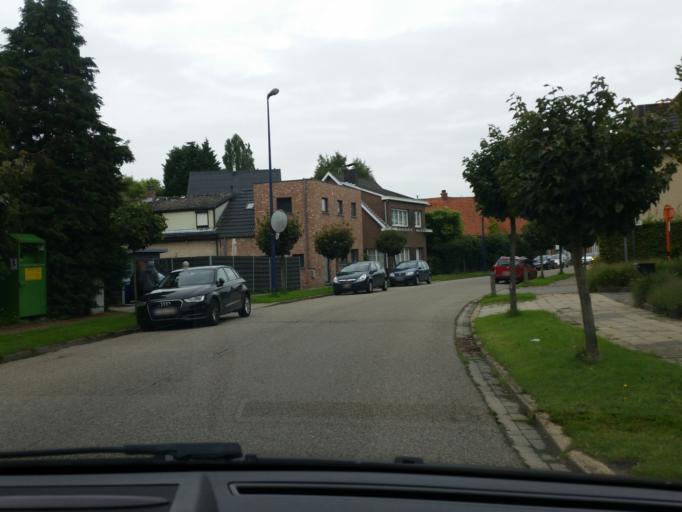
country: BE
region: Flanders
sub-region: Provincie Antwerpen
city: Kontich
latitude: 51.1290
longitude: 4.4400
